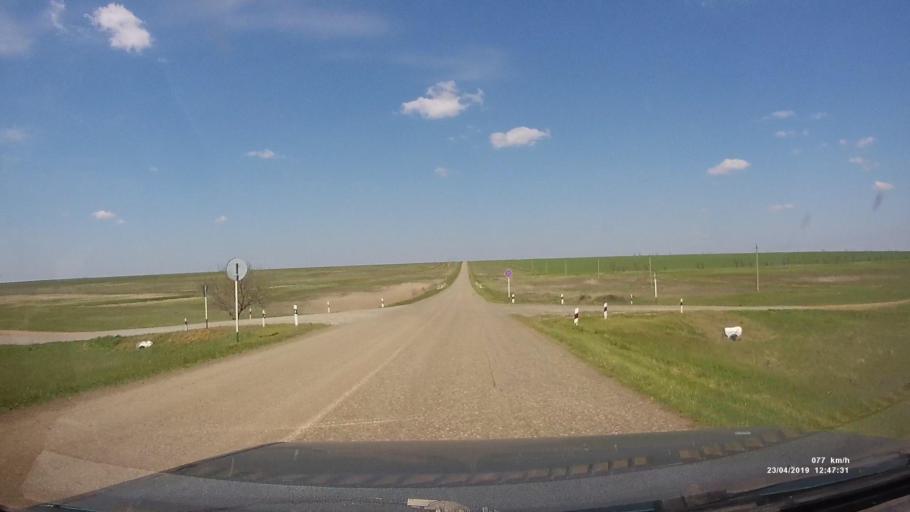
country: RU
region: Kalmykiya
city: Yashalta
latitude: 46.5128
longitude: 42.6389
